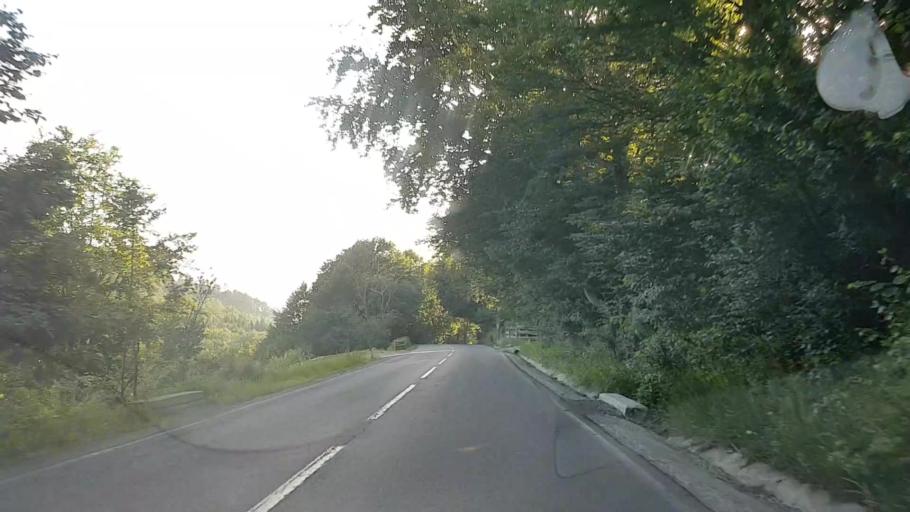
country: RO
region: Harghita
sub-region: Comuna Praid
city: Ocna de Sus
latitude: 46.5732
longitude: 25.2163
